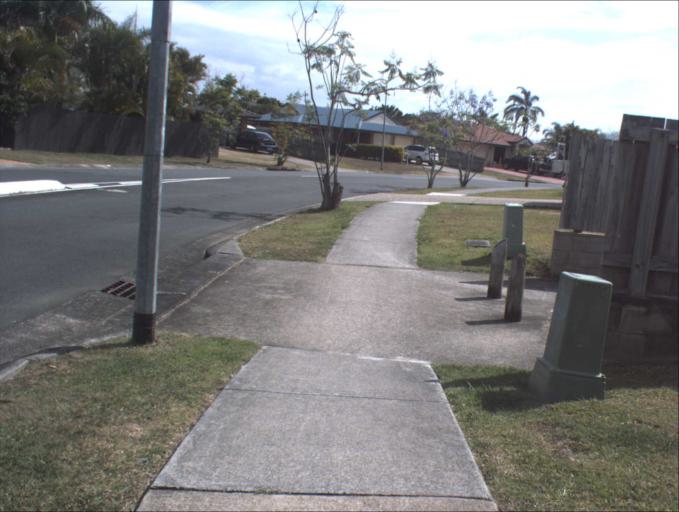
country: AU
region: Queensland
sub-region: Logan
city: Beenleigh
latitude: -27.6822
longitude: 153.1754
